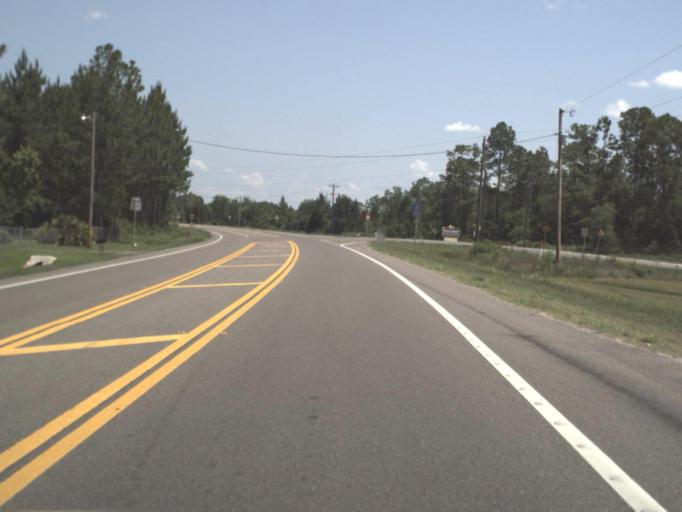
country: US
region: Florida
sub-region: Clay County
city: Keystone Heights
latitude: 29.8233
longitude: -82.0595
